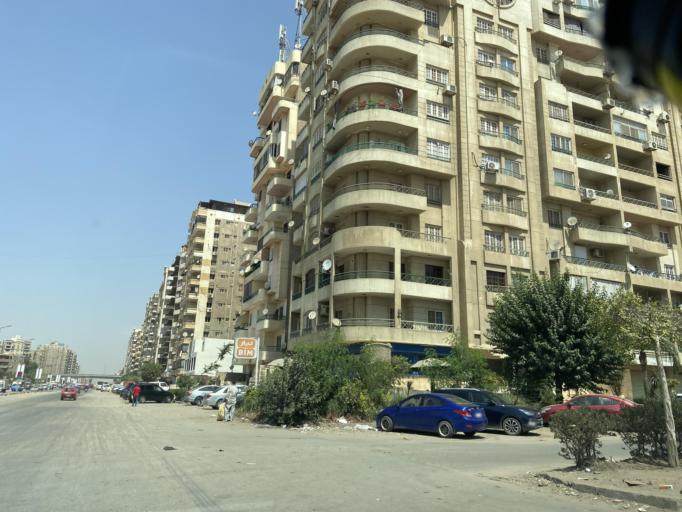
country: EG
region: Muhafazat al Qahirah
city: Cairo
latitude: 30.0442
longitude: 31.3785
